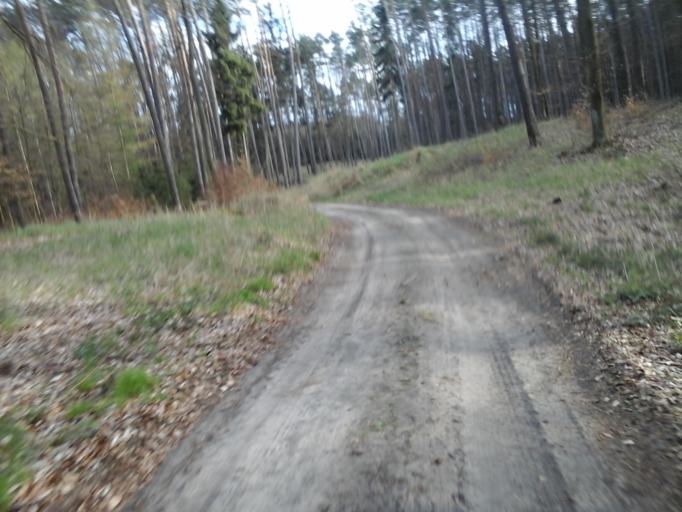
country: PL
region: West Pomeranian Voivodeship
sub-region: Powiat choszczenski
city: Bierzwnik
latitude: 53.0354
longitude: 15.5996
